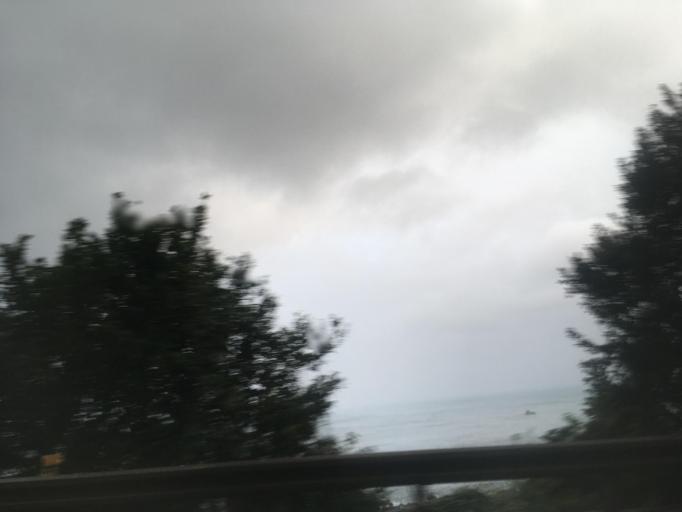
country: TW
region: Taiwan
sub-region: Keelung
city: Keelung
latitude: 24.9830
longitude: 121.9537
